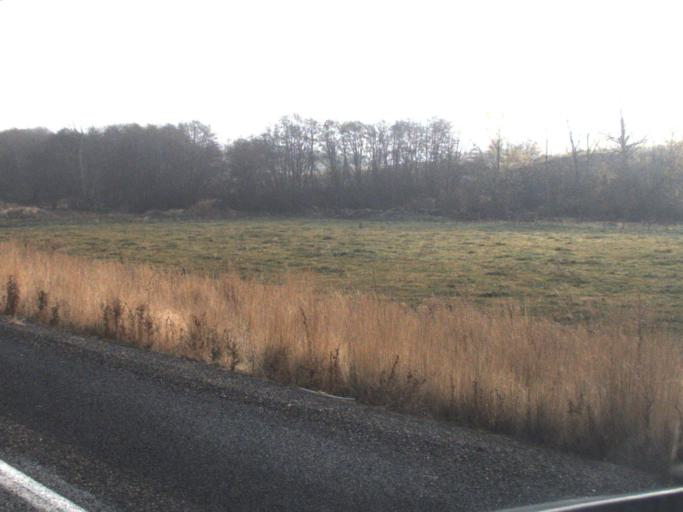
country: US
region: Washington
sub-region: Asotin County
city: Clarkston Heights-Vineland
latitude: 46.4264
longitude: -117.2954
